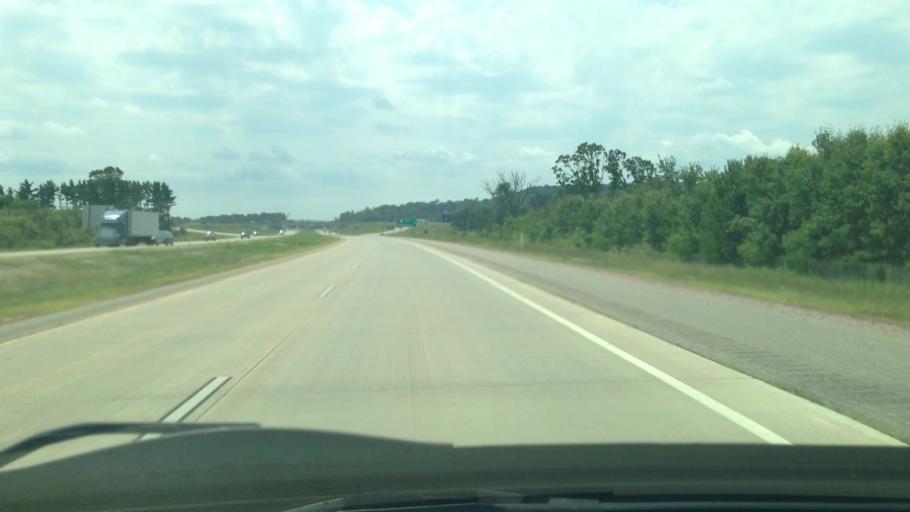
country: US
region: Wisconsin
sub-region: Sauk County
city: West Baraboo
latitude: 43.5211
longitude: -89.7870
